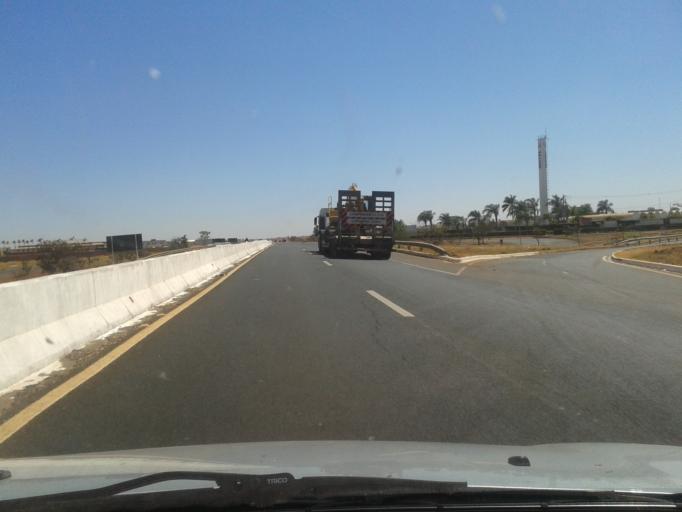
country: BR
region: Minas Gerais
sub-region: Uberlandia
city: Uberlandia
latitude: -18.9264
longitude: -48.2213
